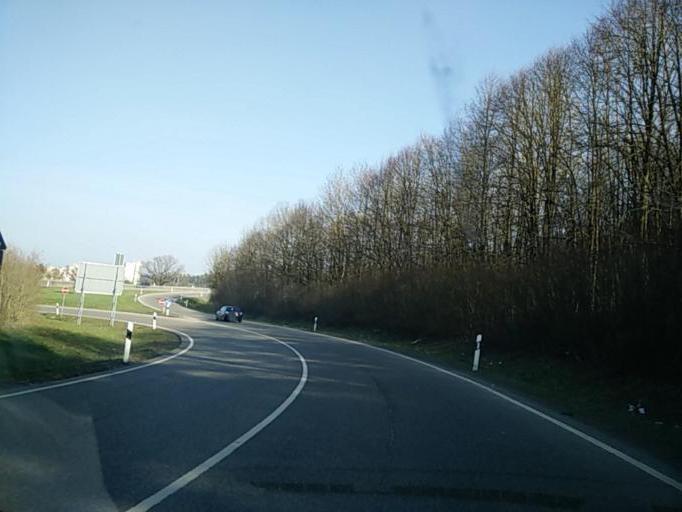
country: DE
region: Baden-Wuerttemberg
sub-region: Regierungsbezirk Stuttgart
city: Boeblingen
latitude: 48.6740
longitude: 8.9778
